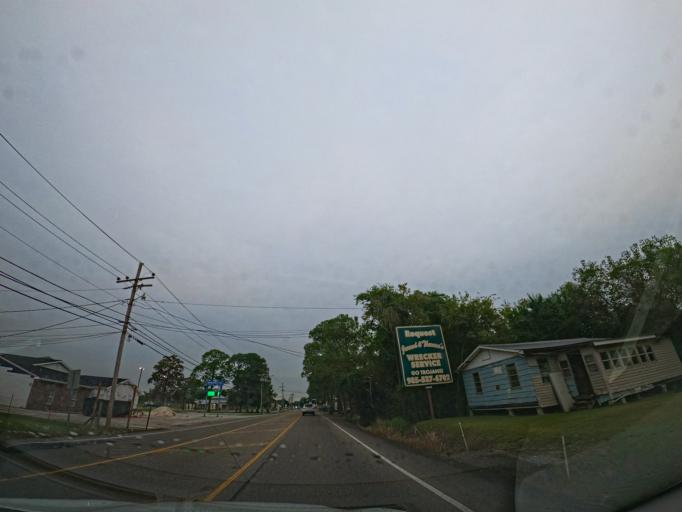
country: US
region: Louisiana
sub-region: Lafourche Parish
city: Mathews
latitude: 29.6999
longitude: -90.5595
